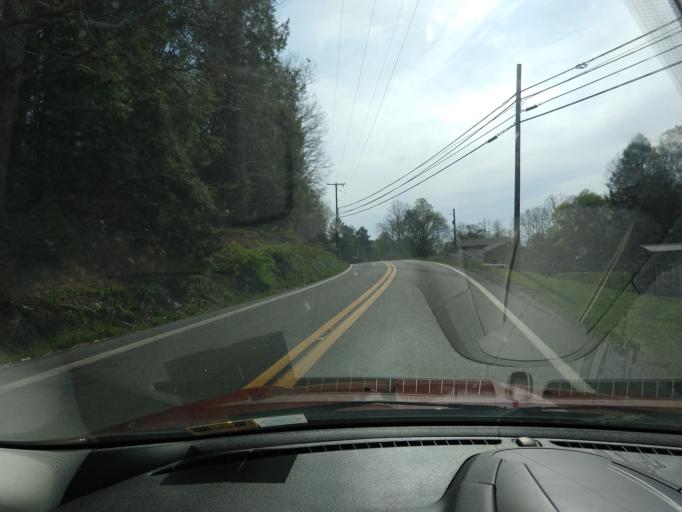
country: US
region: West Virginia
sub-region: Raleigh County
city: Crab Orchard
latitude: 37.7423
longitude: -81.2455
